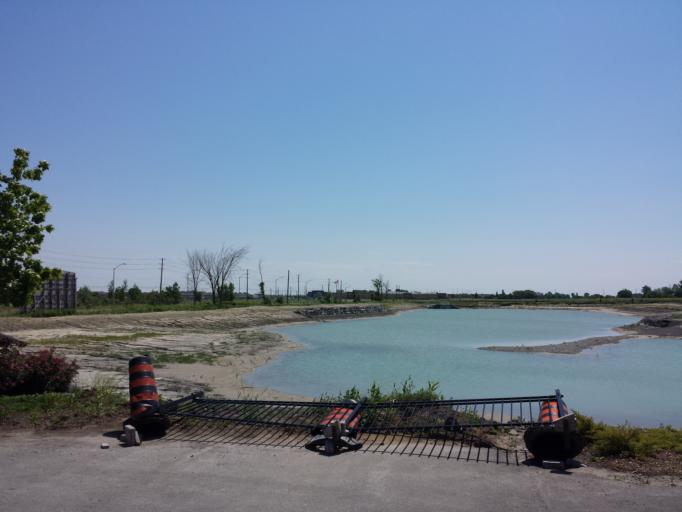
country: CA
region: Ontario
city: Bells Corners
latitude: 45.2794
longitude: -75.8803
